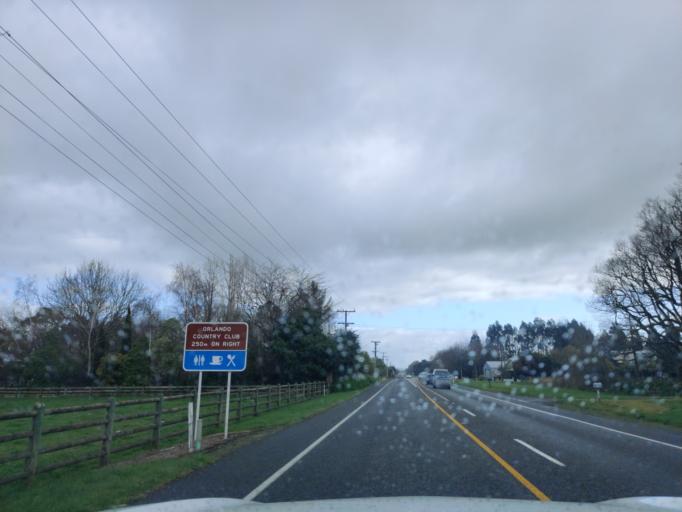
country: NZ
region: Manawatu-Wanganui
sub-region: Palmerston North City
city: Palmerston North
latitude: -40.3280
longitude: 175.5849
